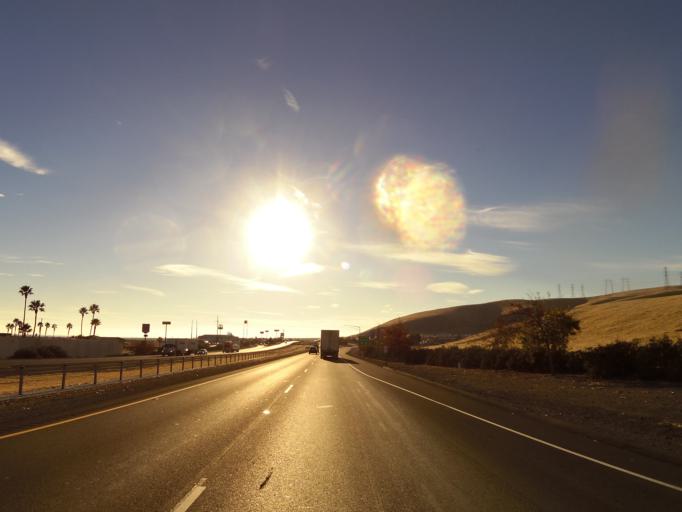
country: US
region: California
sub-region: Stanislaus County
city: Patterson
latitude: 37.5434
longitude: -121.2723
